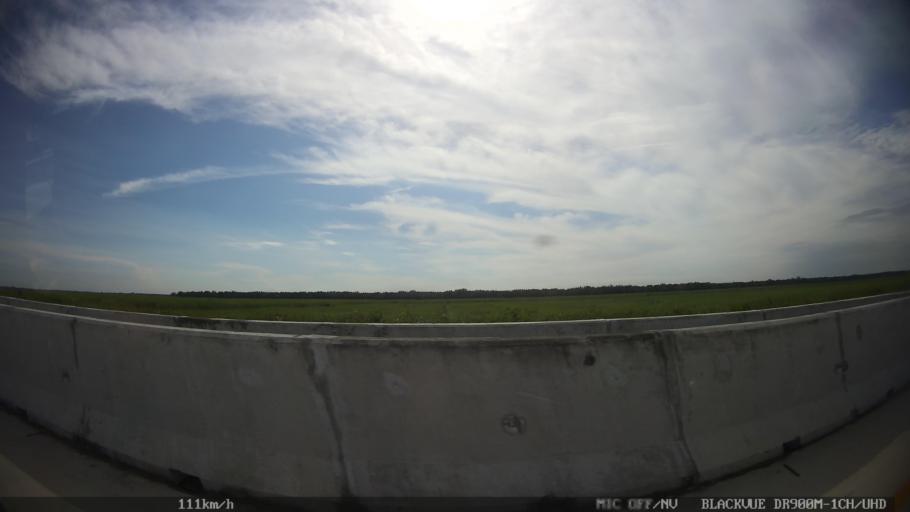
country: ID
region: North Sumatra
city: Binjai
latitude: 3.6601
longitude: 98.5328
